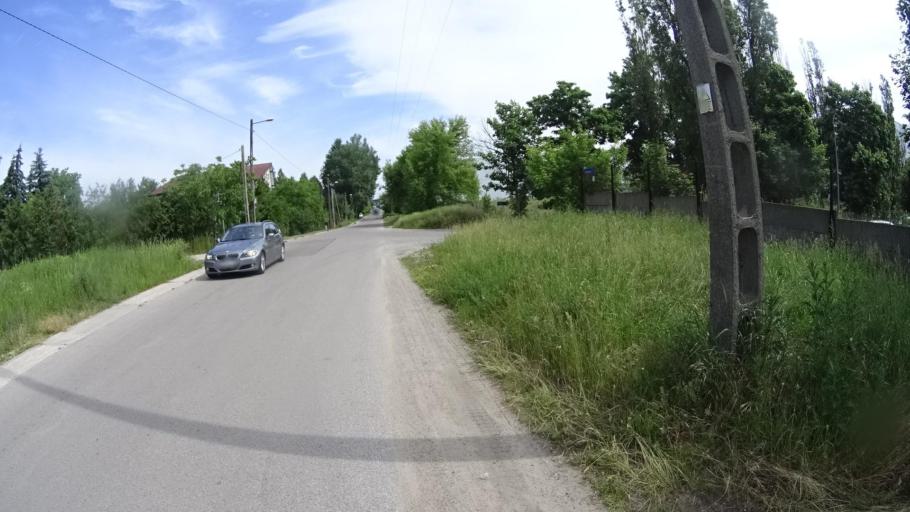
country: PL
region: Masovian Voivodeship
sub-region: Powiat pruszkowski
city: Raszyn
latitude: 52.1697
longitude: 20.9294
